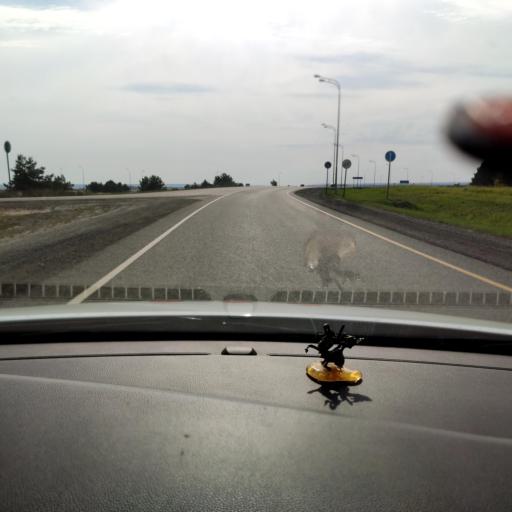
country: RU
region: Tatarstan
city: Verkhniy Uslon
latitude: 55.7091
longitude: 48.8893
